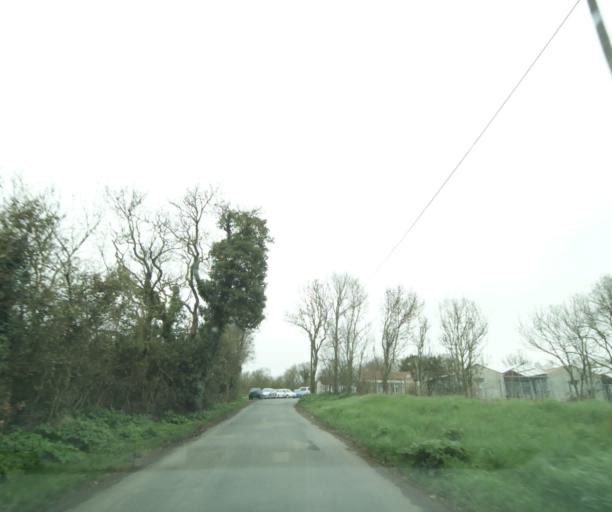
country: FR
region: Poitou-Charentes
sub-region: Departement de la Charente-Maritime
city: Lagord
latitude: 46.1830
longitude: -1.1378
